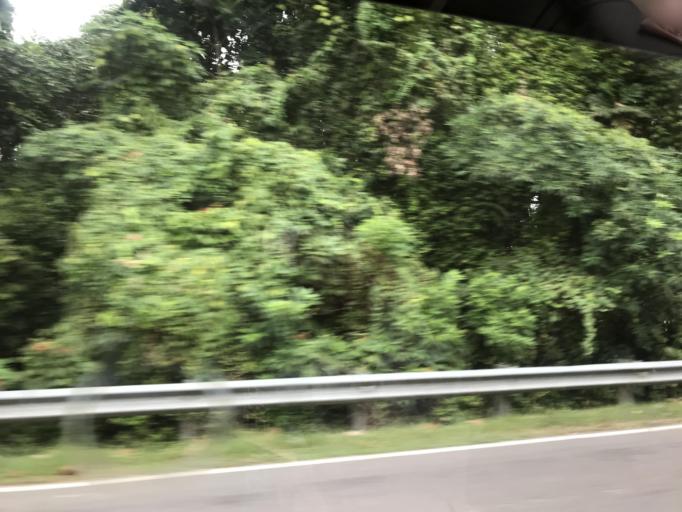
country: MY
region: Kelantan
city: Kota Bharu
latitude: 6.1510
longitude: 102.2287
